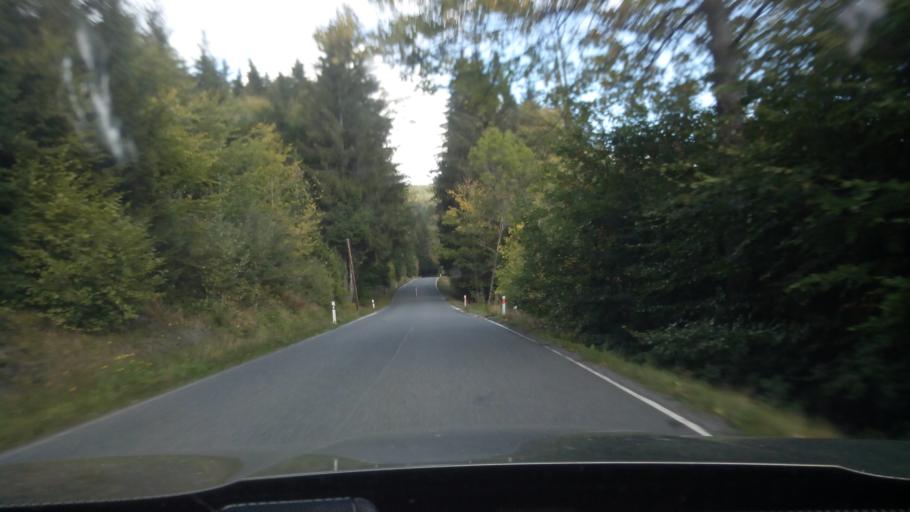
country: CZ
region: Plzensky
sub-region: Okres Klatovy
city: Kasperske Hory
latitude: 49.1392
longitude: 13.5912
